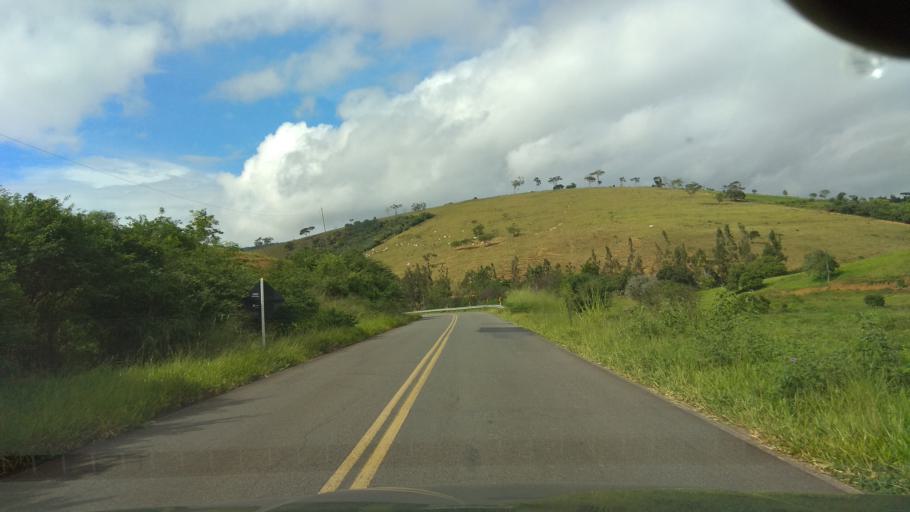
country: BR
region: Bahia
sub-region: Ubaira
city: Ubaira
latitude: -13.2613
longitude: -39.7012
